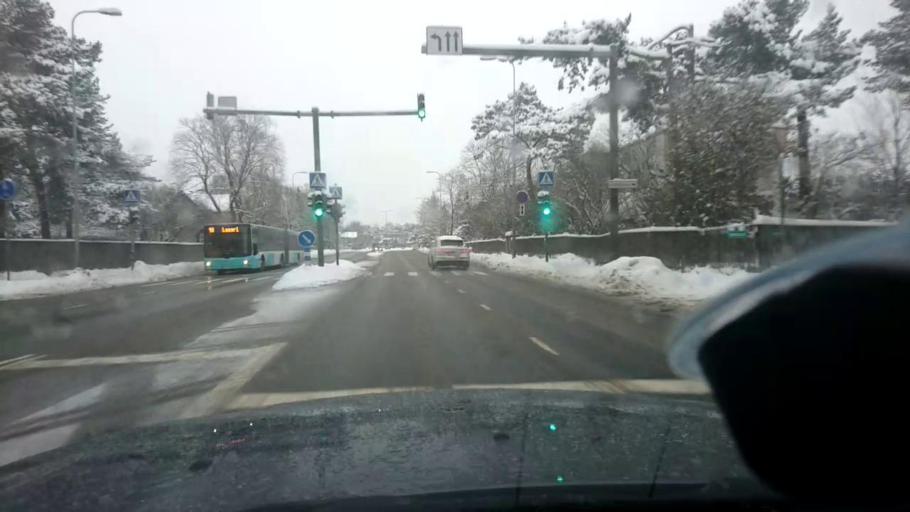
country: EE
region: Harju
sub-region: Tallinna linn
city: Tallinn
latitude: 59.3870
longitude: 24.7154
